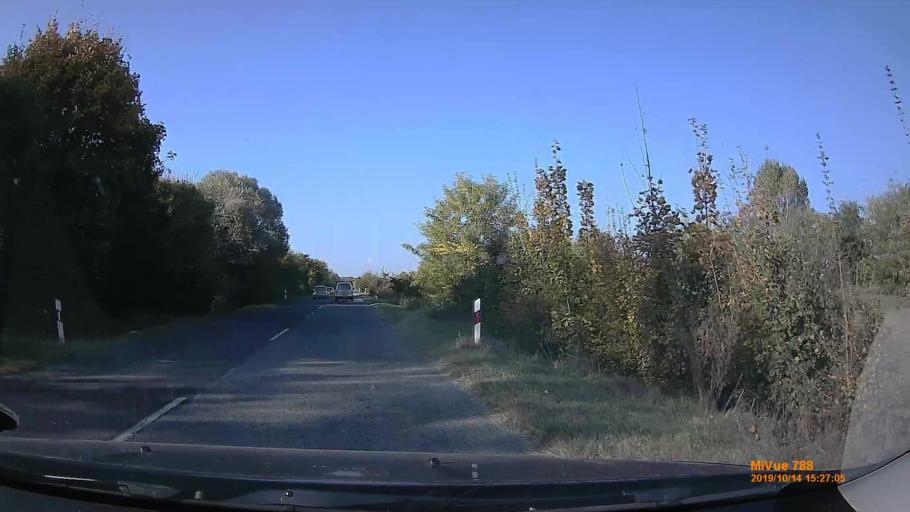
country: HU
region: Pest
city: Ecser
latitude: 47.4262
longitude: 19.3091
